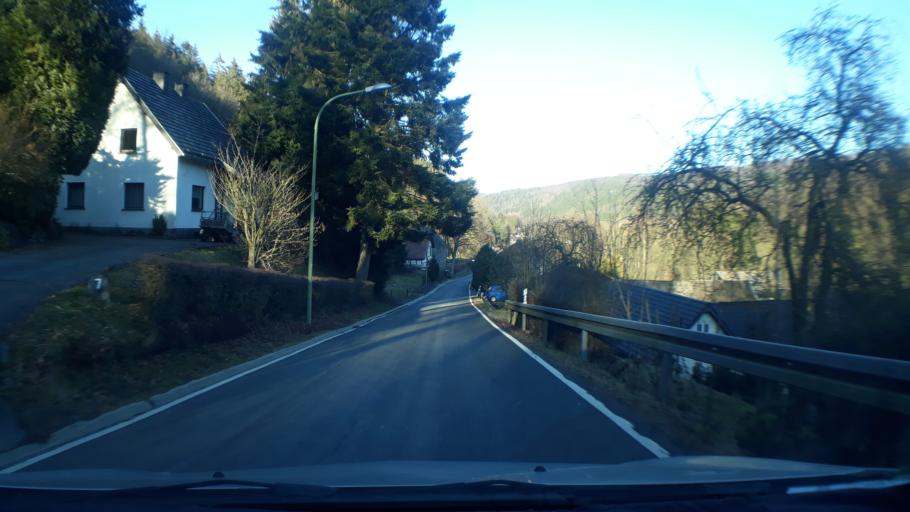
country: DE
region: North Rhine-Westphalia
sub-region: Regierungsbezirk Koln
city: Simmerath
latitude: 50.5629
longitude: 6.3242
